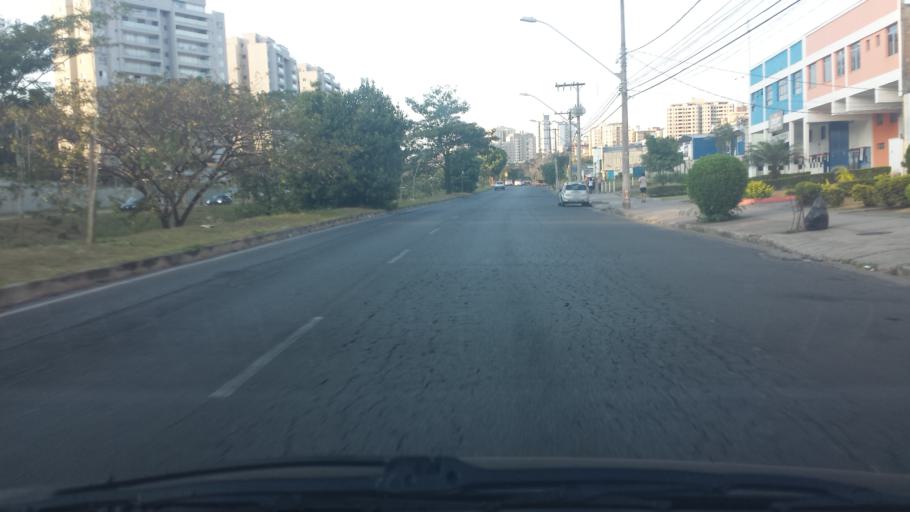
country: BR
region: Minas Gerais
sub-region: Belo Horizonte
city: Belo Horizonte
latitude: -19.8801
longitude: -43.9928
